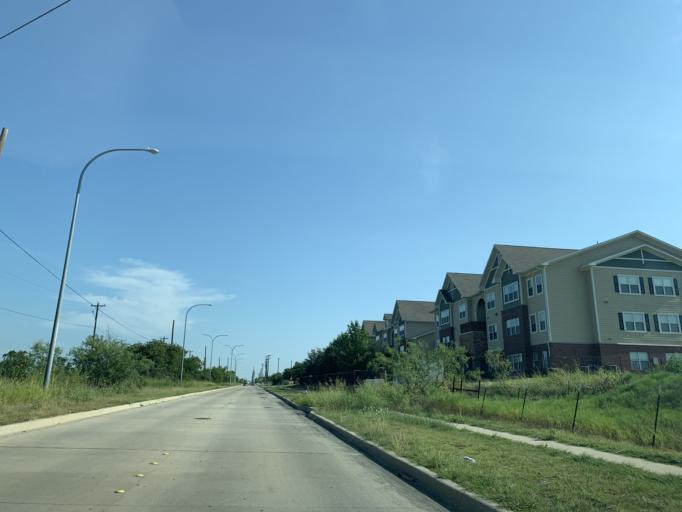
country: US
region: Texas
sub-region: Tarrant County
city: Blue Mound
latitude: 32.8872
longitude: -97.3069
